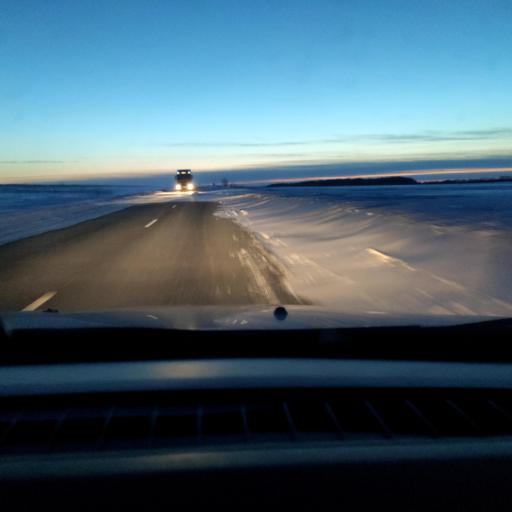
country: RU
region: Samara
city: Georgiyevka
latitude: 53.3058
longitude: 50.8085
